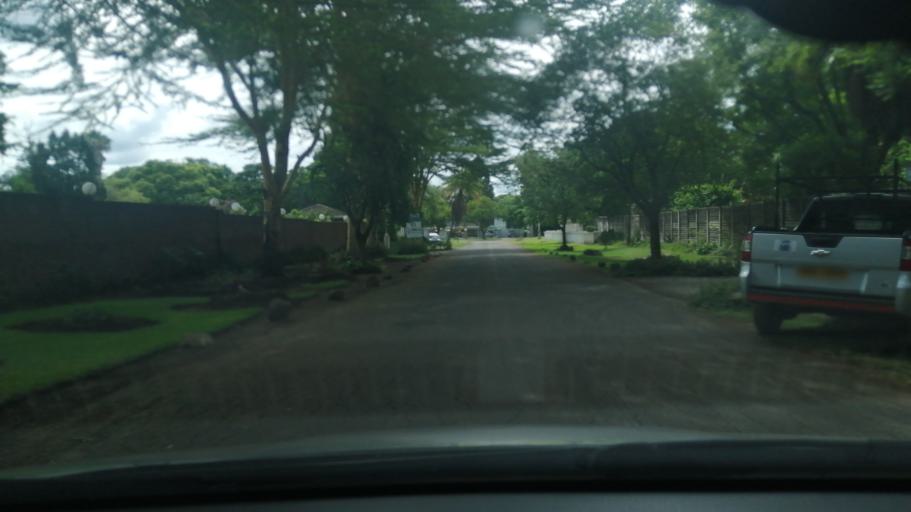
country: ZW
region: Harare
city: Harare
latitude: -17.8007
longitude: 31.0437
